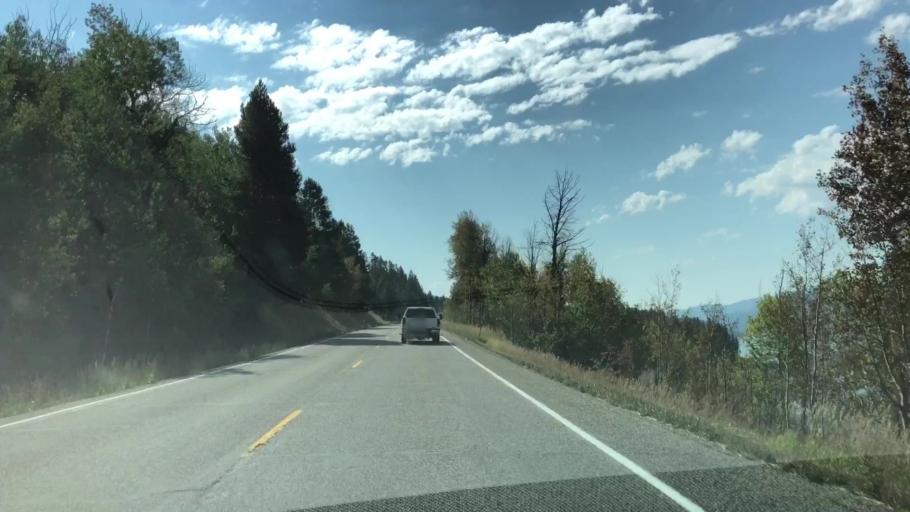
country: US
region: Idaho
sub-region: Teton County
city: Victor
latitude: 43.2918
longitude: -111.1241
